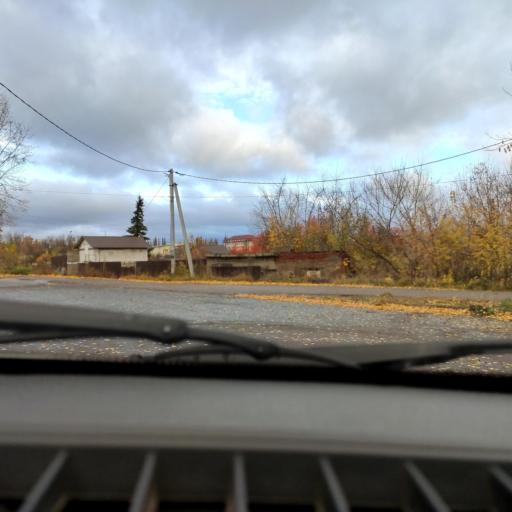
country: RU
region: Bashkortostan
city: Avdon
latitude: 54.6783
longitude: 55.8071
